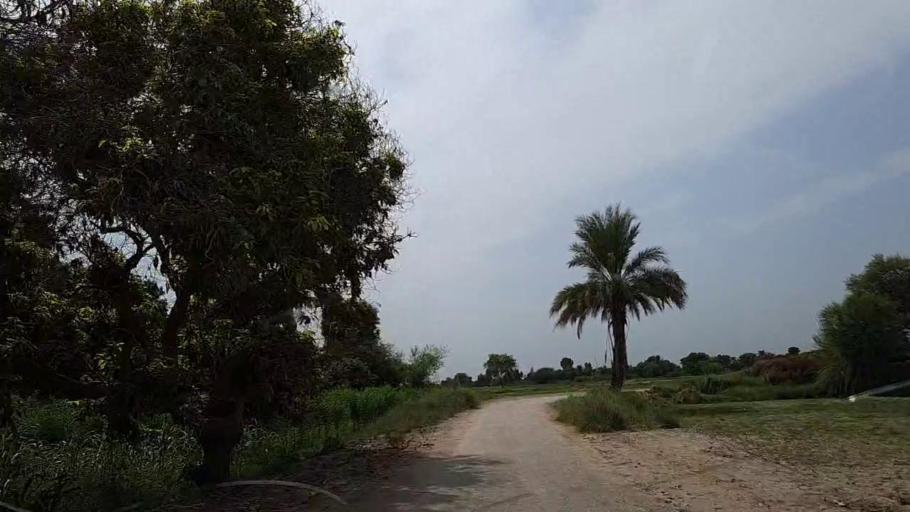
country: PK
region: Sindh
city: Tharu Shah
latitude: 26.8959
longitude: 68.0784
